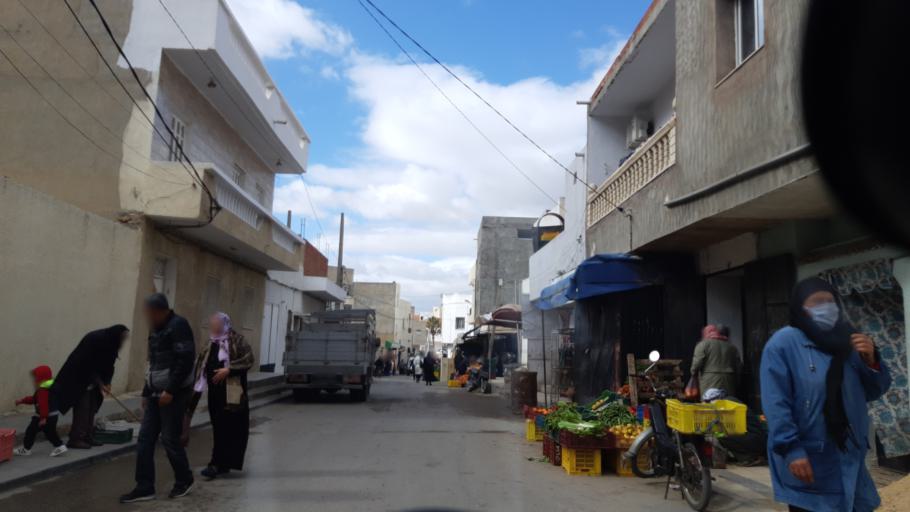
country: TN
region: Susah
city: Akouda
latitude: 35.8711
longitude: 10.5327
